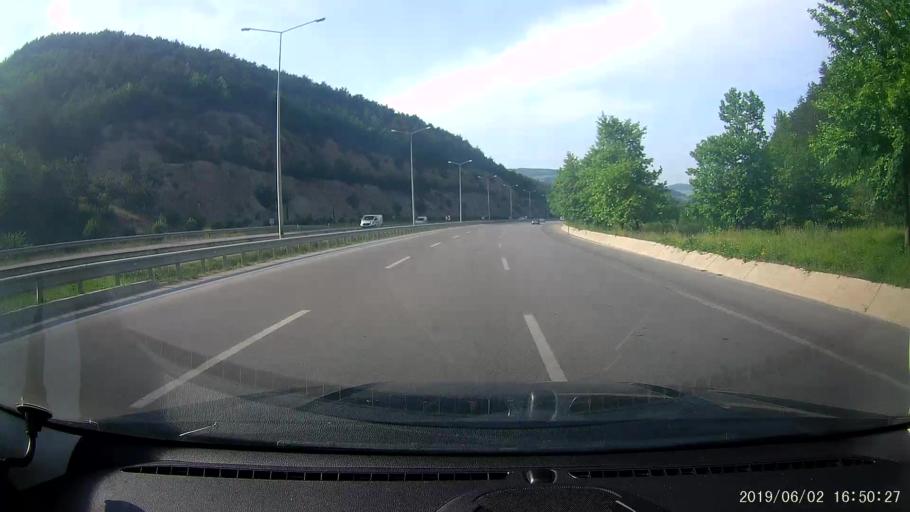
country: TR
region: Samsun
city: Samsun
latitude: 41.2549
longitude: 36.1736
